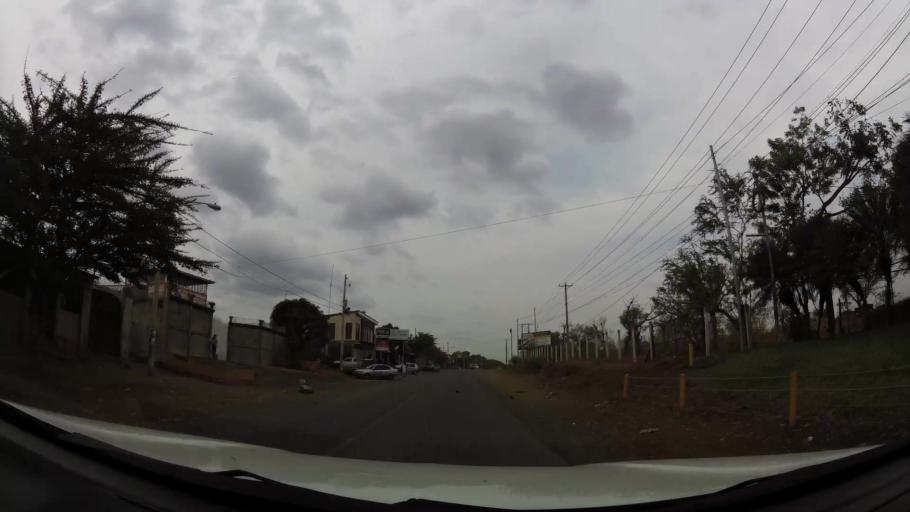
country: NI
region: Managua
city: Managua
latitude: 12.1233
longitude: -86.1886
